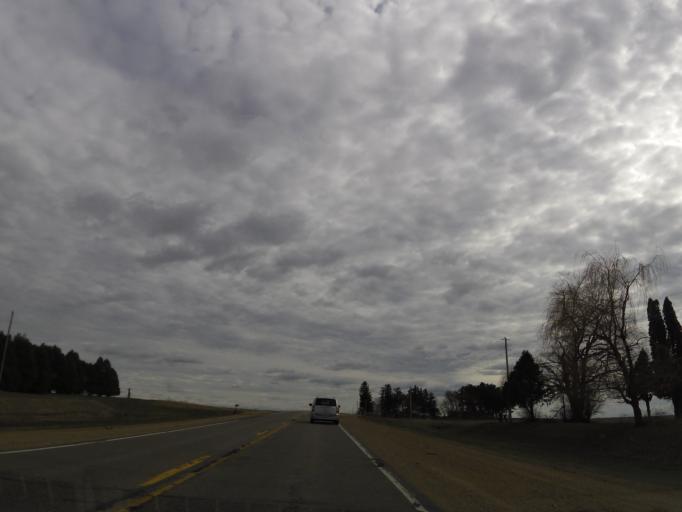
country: US
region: Iowa
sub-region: Chickasaw County
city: New Hampton
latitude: 43.2221
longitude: -92.2985
